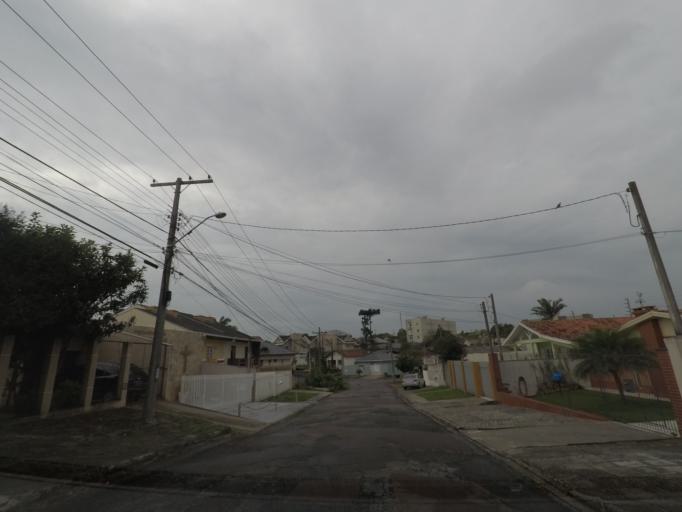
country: BR
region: Parana
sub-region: Curitiba
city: Curitiba
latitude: -25.4701
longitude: -49.3099
